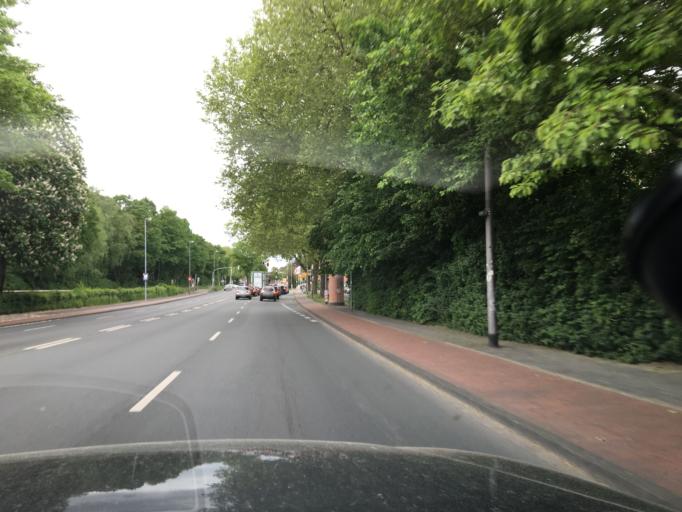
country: DE
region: North Rhine-Westphalia
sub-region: Regierungsbezirk Munster
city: Muenster
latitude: 51.9680
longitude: 7.6619
